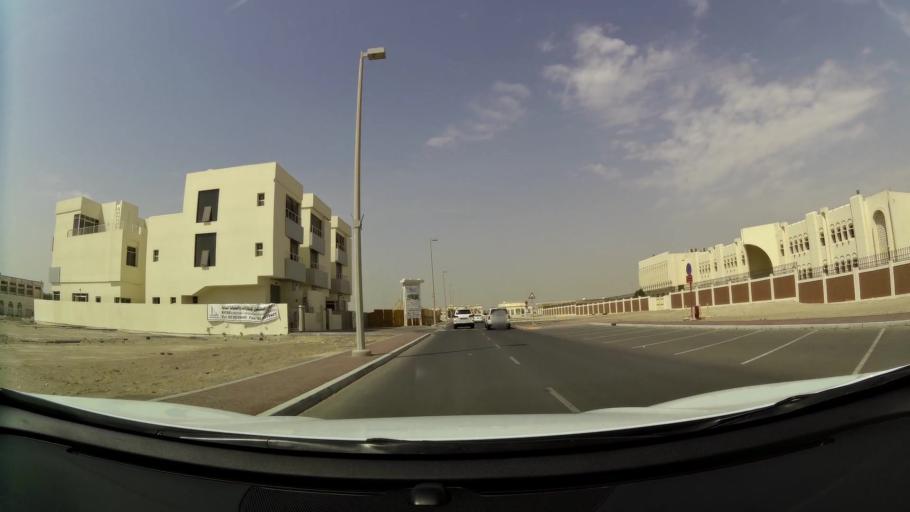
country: AE
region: Abu Dhabi
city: Abu Dhabi
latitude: 24.2977
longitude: 54.6339
